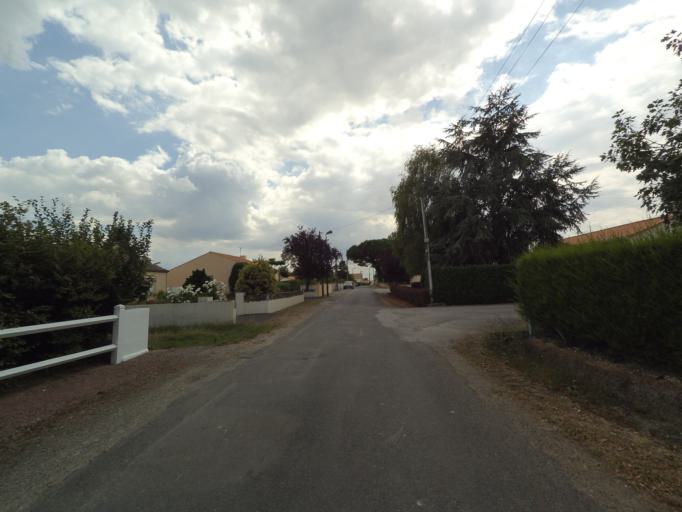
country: FR
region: Pays de la Loire
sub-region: Departement de la Loire-Atlantique
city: Vieillevigne
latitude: 46.9703
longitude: -1.4237
